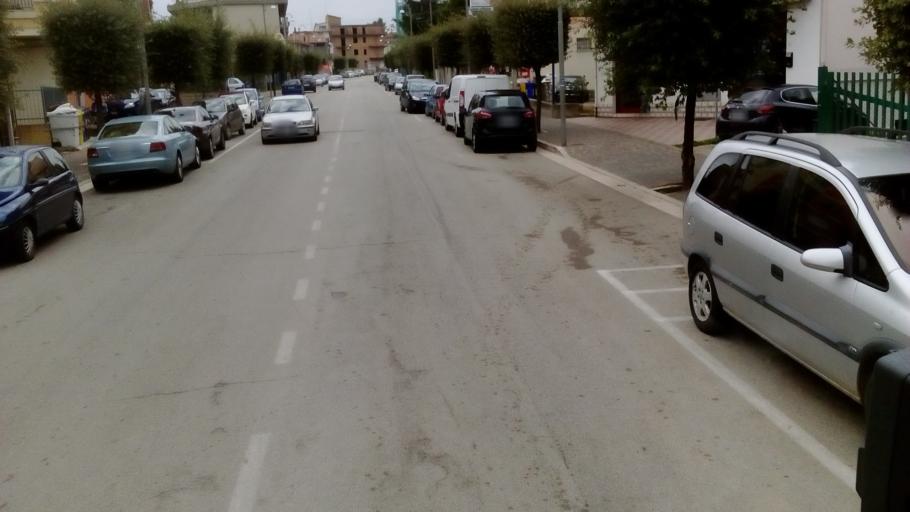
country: IT
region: Abruzzo
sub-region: Provincia di Chieti
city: San Salvo
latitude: 42.0529
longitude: 14.7328
